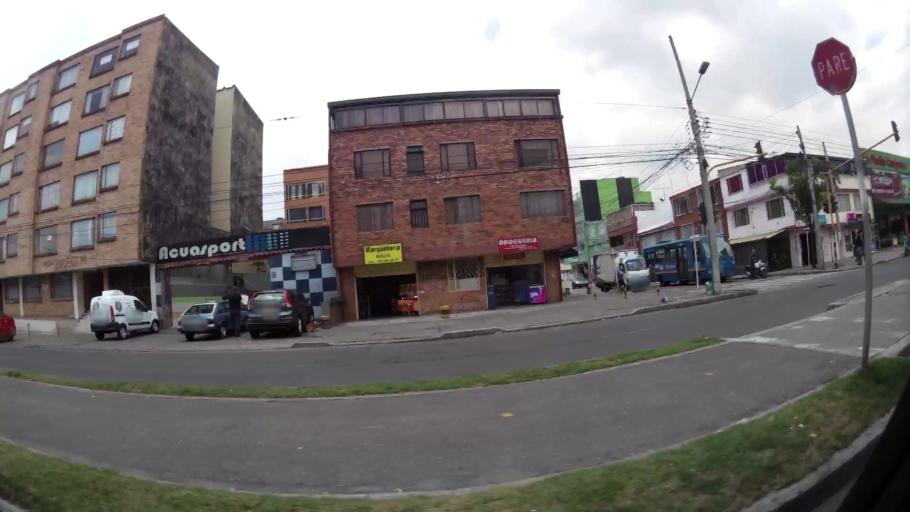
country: CO
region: Cundinamarca
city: La Calera
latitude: 4.7409
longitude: -74.0404
